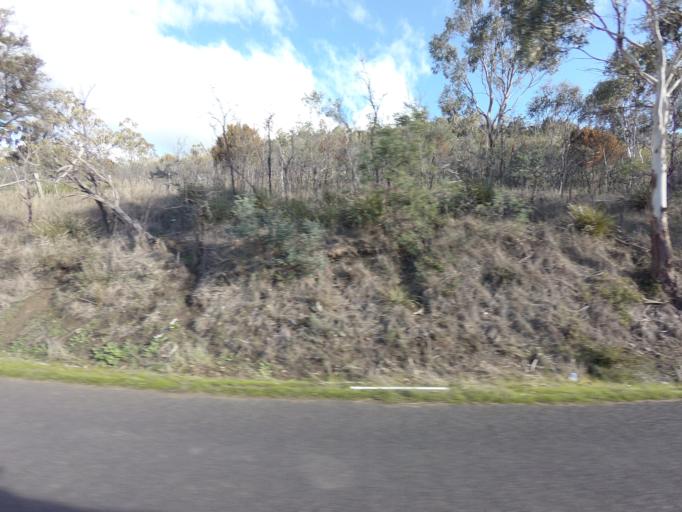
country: AU
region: Tasmania
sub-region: Derwent Valley
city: New Norfolk
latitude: -42.7458
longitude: 147.0415
